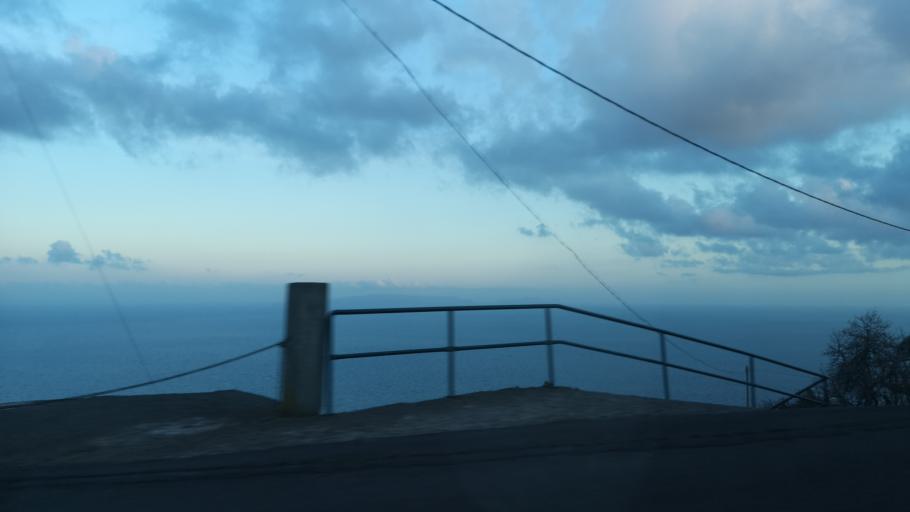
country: PT
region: Madeira
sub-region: Santa Cruz
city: Santa Cruz
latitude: 32.6704
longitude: -16.8162
